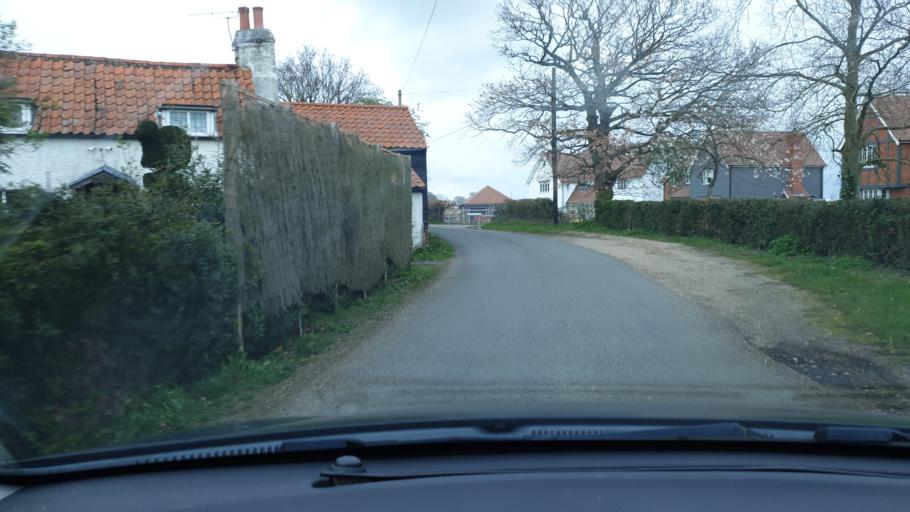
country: GB
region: England
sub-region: Essex
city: Great Bentley
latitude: 51.8905
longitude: 1.1104
